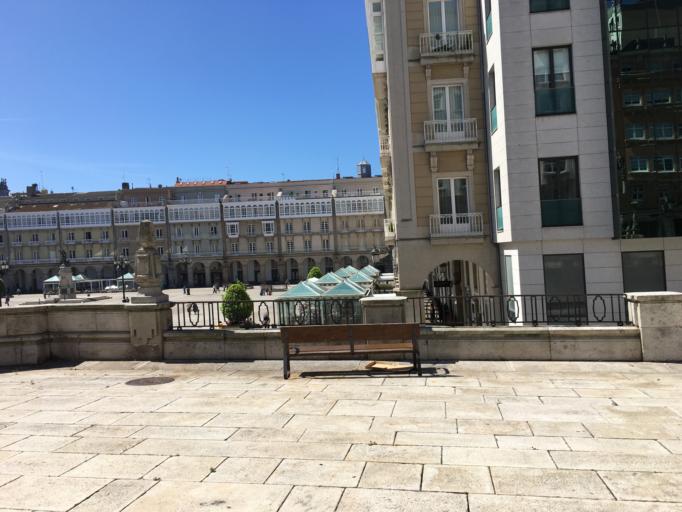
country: ES
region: Galicia
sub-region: Provincia da Coruna
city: A Coruna
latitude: 43.3715
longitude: -8.3966
